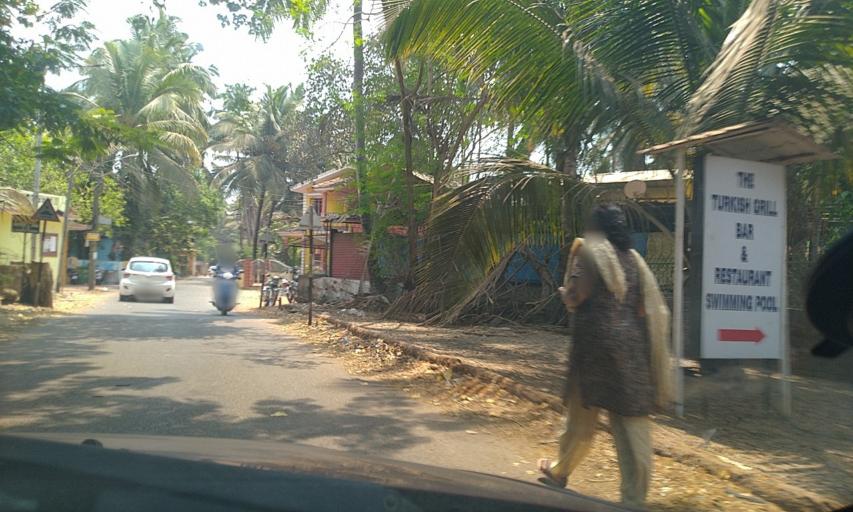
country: IN
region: Goa
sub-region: North Goa
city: Saligao
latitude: 15.5541
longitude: 73.7791
